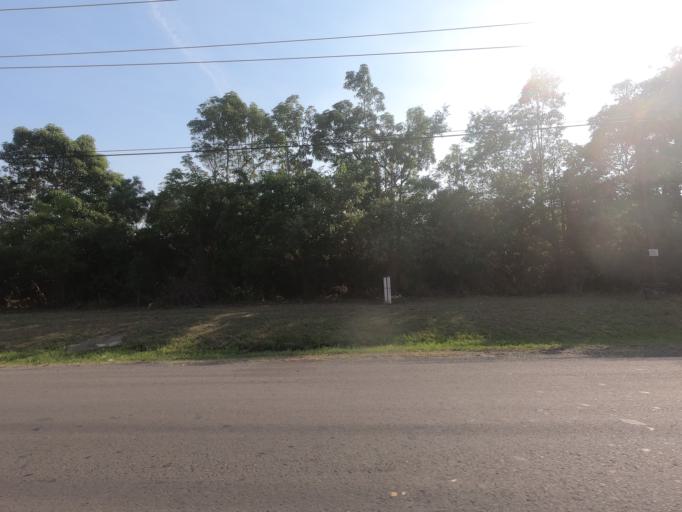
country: AU
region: New South Wales
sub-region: Wollongong
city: Mount Saint Thomas
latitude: -34.4511
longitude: 150.8559
